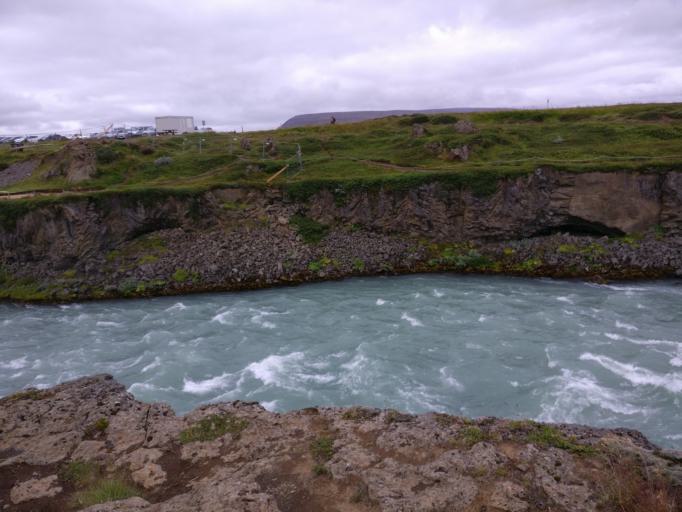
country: IS
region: Northeast
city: Laugar
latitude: 65.6839
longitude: -17.5466
